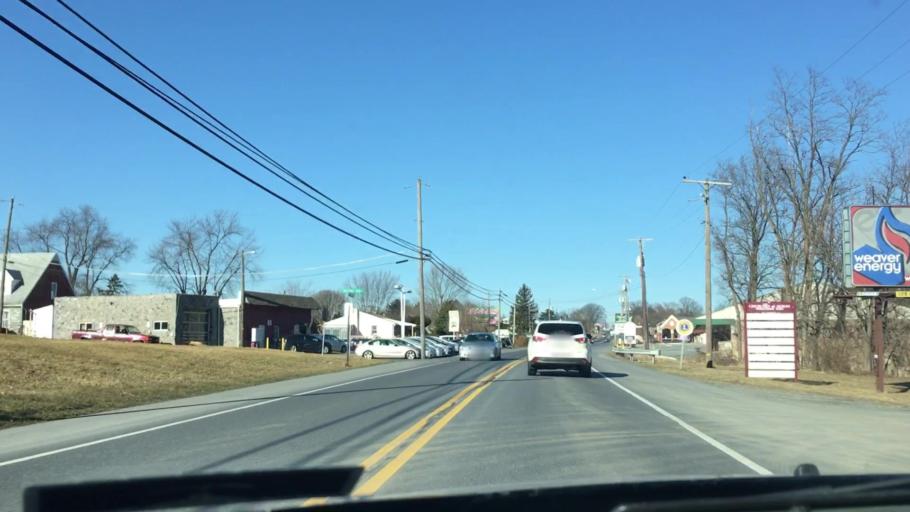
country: US
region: Pennsylvania
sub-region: Lancaster County
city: Akron
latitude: 40.1489
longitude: -76.2090
